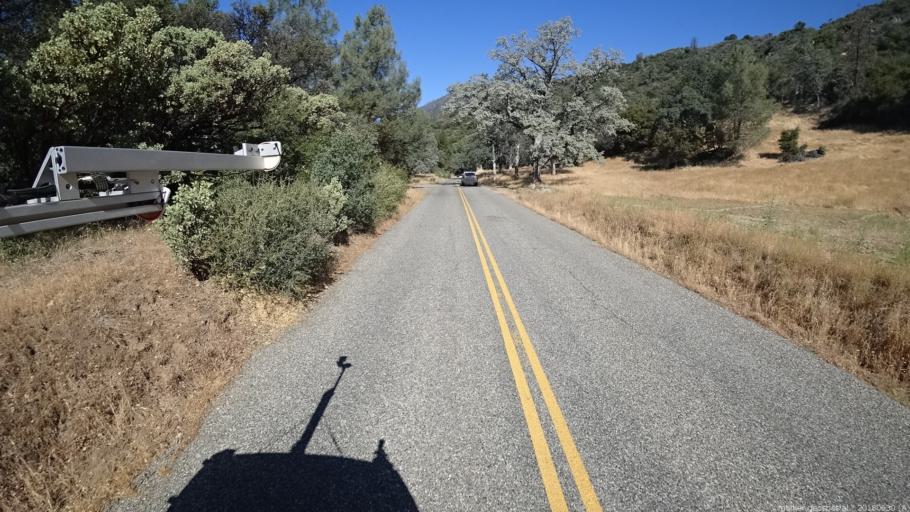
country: US
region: California
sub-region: Fresno County
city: Auberry
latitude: 37.2159
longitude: -119.3547
